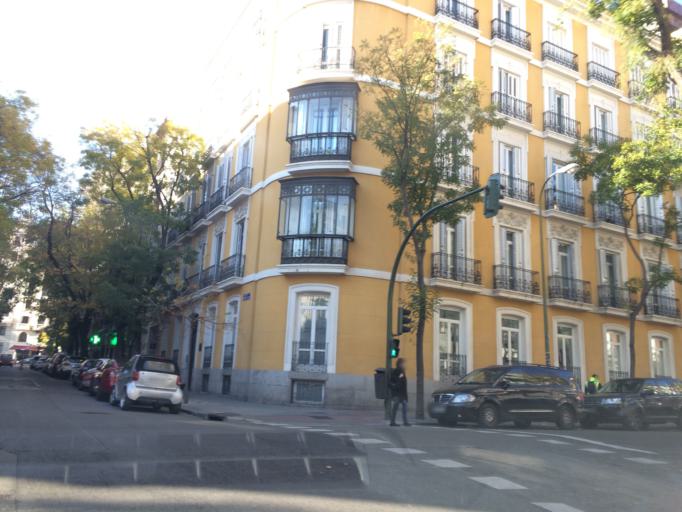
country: ES
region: Madrid
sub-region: Provincia de Madrid
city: Chamberi
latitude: 40.4282
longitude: -3.6935
